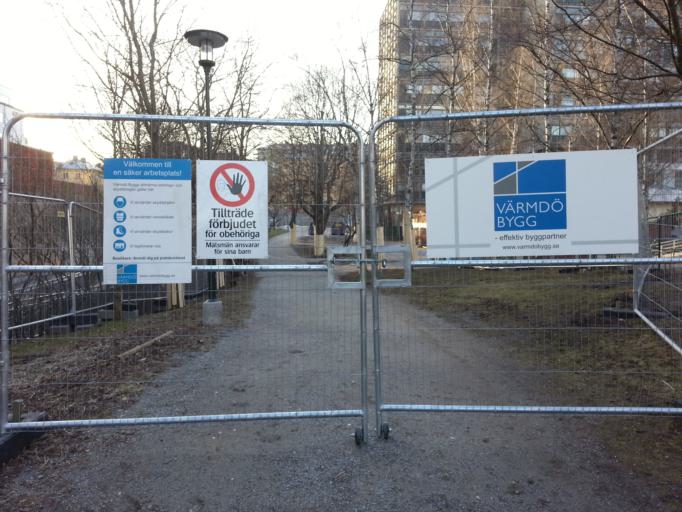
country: SE
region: Stockholm
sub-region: Solna Kommun
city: Solna
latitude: 59.3332
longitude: 18.0265
